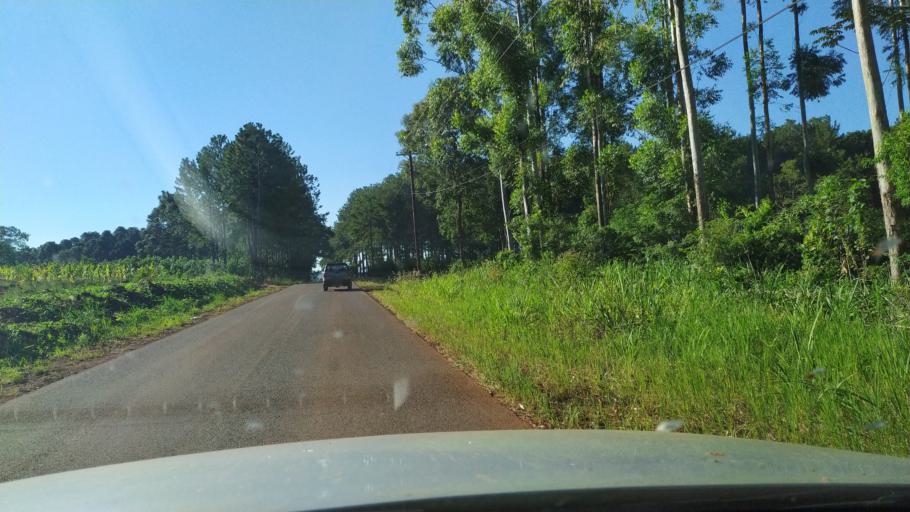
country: AR
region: Misiones
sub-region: Departamento de Montecarlo
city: Montecarlo
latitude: -26.5853
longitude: -54.7244
